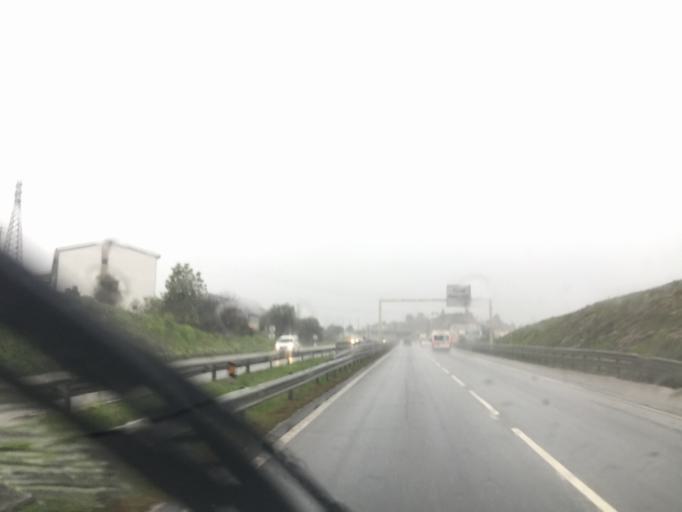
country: PT
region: Coimbra
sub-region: Coimbra
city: Coimbra
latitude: 40.2345
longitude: -8.4359
